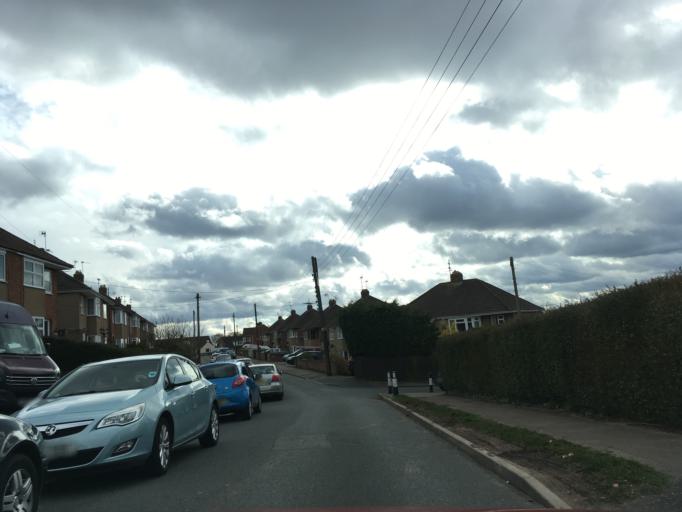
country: GB
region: England
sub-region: Gloucestershire
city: Cinderford
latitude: 51.8183
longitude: -2.4997
